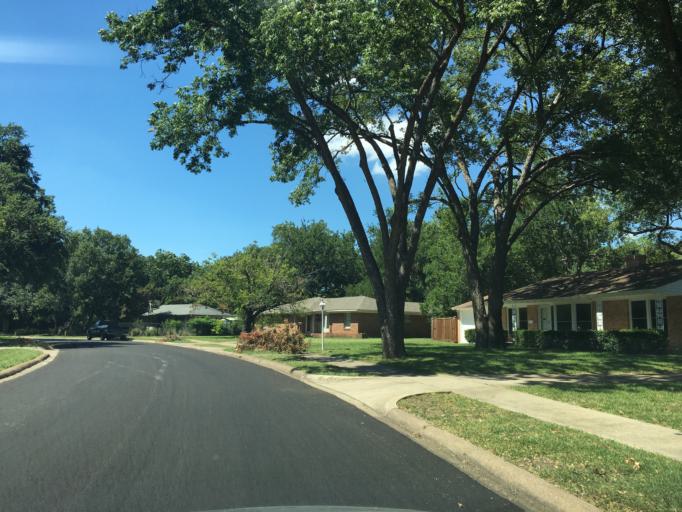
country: US
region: Texas
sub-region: Dallas County
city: Highland Park
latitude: 32.8387
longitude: -96.7001
